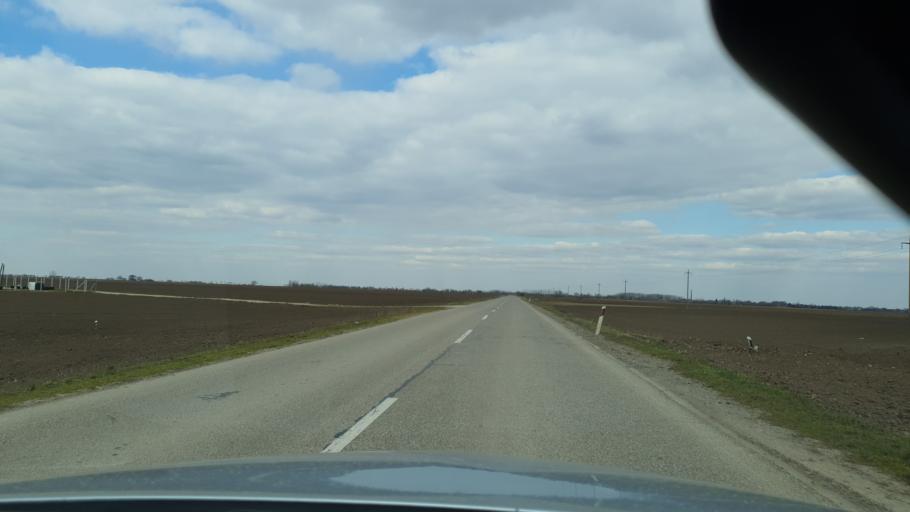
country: RS
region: Autonomna Pokrajina Vojvodina
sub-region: Juznobacki Okrug
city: Bac
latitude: 45.4329
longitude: 19.3108
